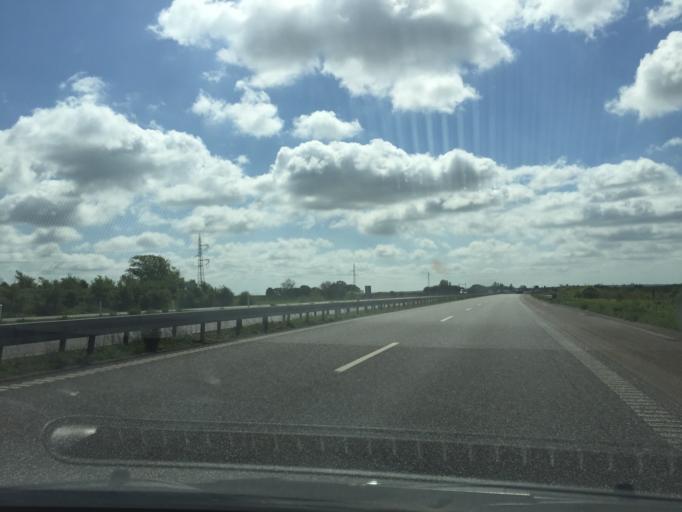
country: DK
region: Zealand
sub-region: Guldborgsund Kommune
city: Sundby
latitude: 54.8404
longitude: 11.8180
